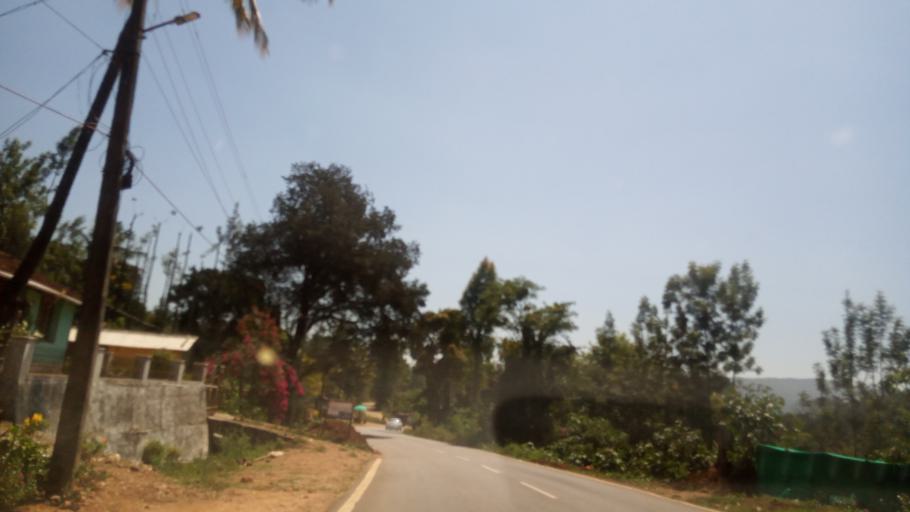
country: IN
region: Karnataka
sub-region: Chikmagalur
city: Chikmagalur
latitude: 13.4413
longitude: 75.8037
